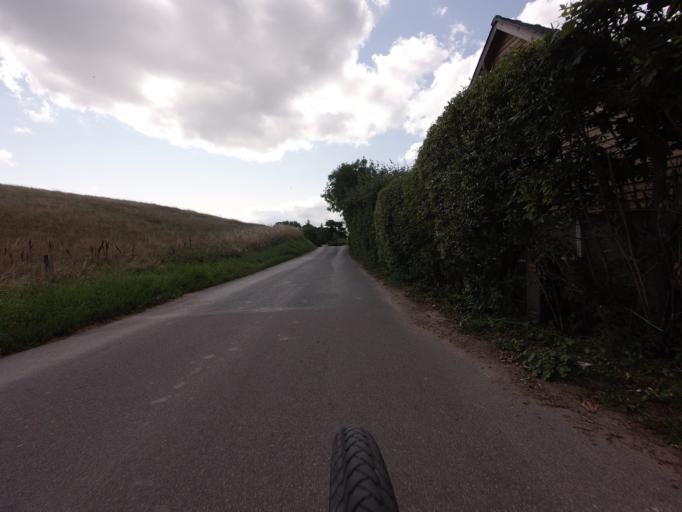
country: DK
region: Zealand
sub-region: Vordingborg Kommune
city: Stege
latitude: 54.9606
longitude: 12.5269
